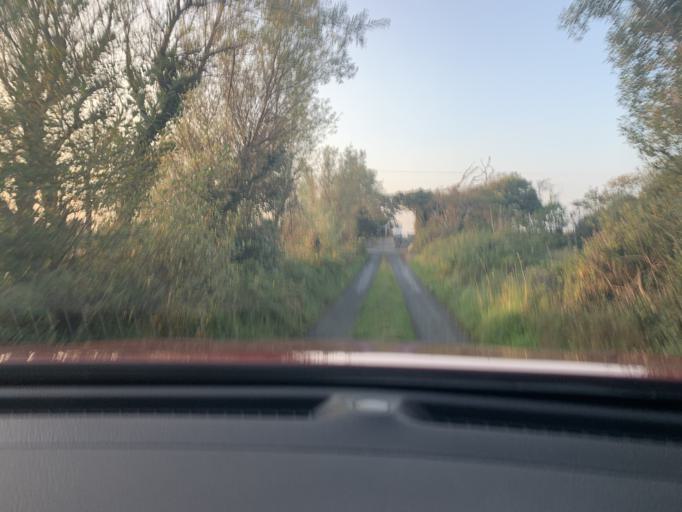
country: IE
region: Connaught
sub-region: County Leitrim
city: Kinlough
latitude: 54.4574
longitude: -8.3992
